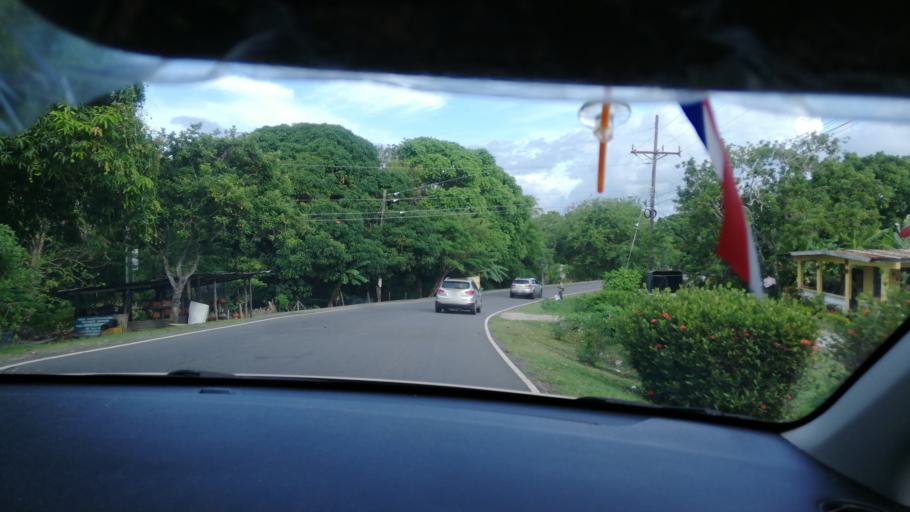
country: PA
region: Panama
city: Las Colinas
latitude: 8.5221
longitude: -80.0372
